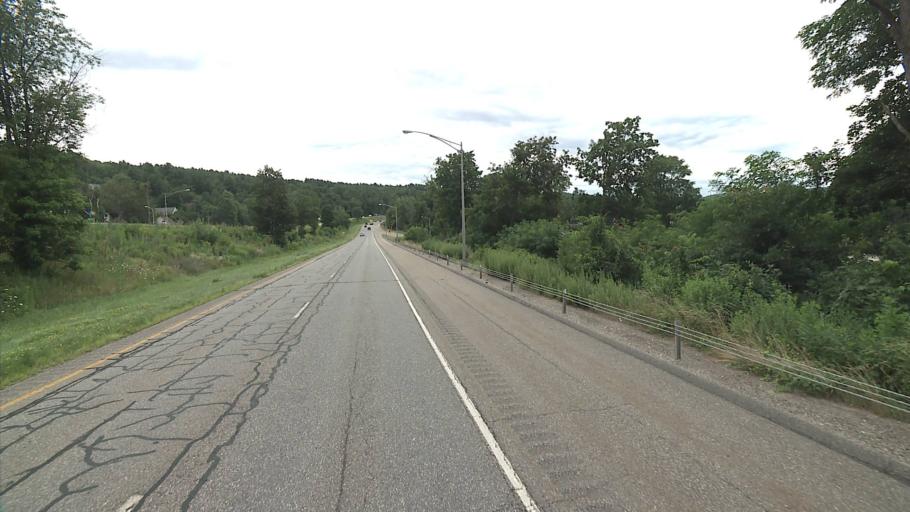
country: US
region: Connecticut
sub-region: Litchfield County
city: Torrington
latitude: 41.7949
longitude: -73.1109
